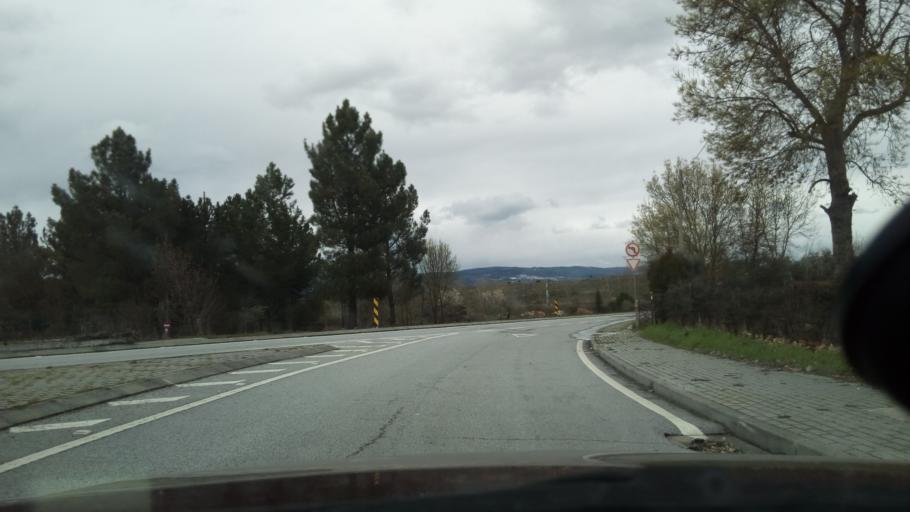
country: PT
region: Guarda
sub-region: Fornos de Algodres
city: Fornos de Algodres
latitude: 40.5306
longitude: -7.5759
